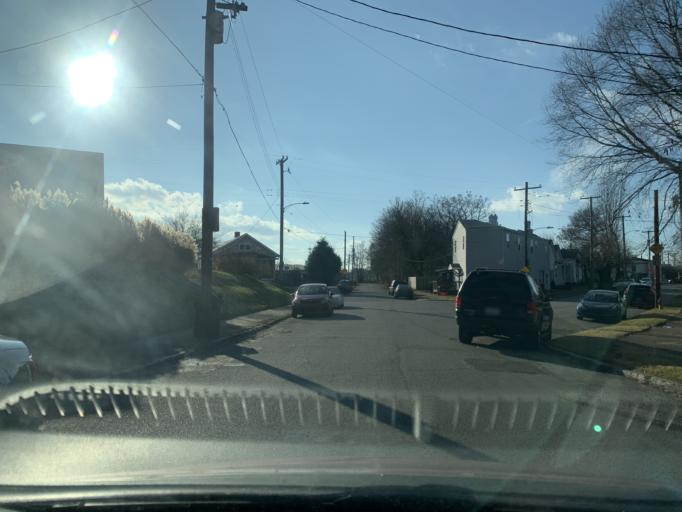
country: US
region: Kentucky
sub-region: Jefferson County
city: Audubon Park
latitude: 38.2320
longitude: -85.7378
